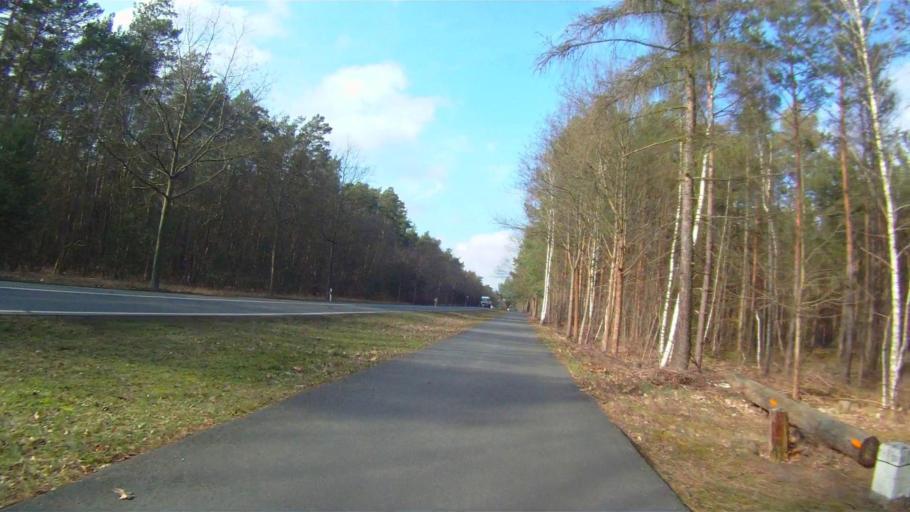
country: DE
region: Brandenburg
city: Zeuthen
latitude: 52.3957
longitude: 13.6121
